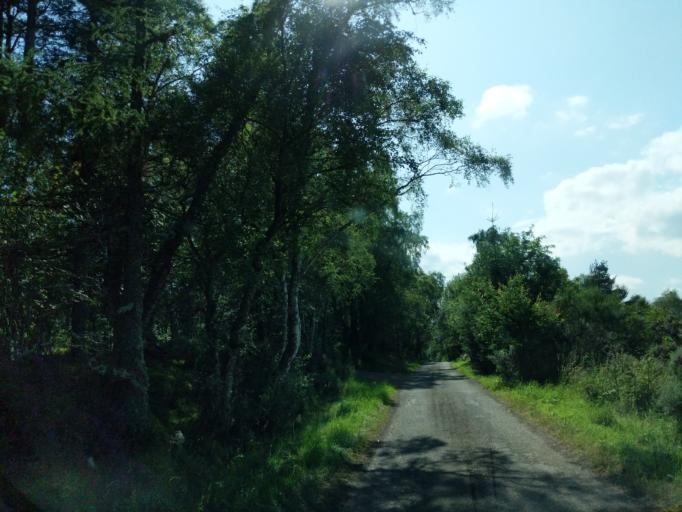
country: GB
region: Scotland
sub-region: Moray
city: Fochabers
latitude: 57.5600
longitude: -3.1261
